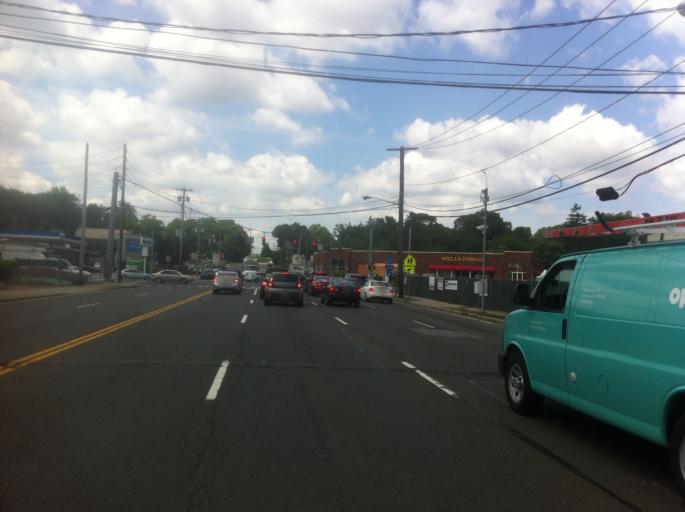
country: US
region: New York
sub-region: Nassau County
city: Greenvale
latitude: 40.8123
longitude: -73.6187
